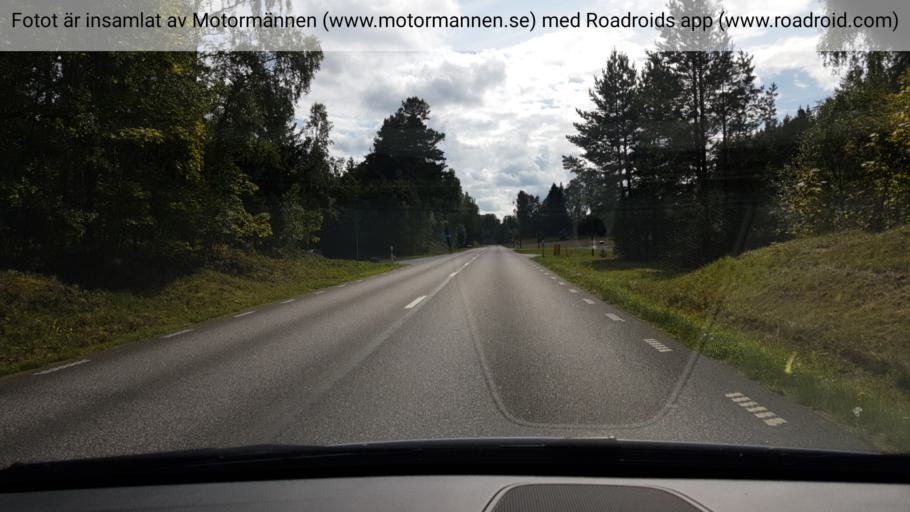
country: SE
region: Joenkoeping
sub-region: Mullsjo Kommun
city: Mullsjoe
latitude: 58.0582
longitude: 13.8055
